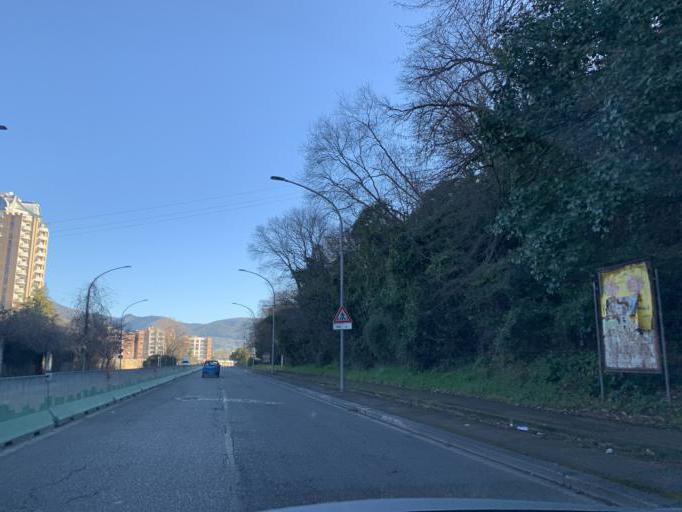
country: IT
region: Umbria
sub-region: Provincia di Terni
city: Terni
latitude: 42.5563
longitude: 12.6534
